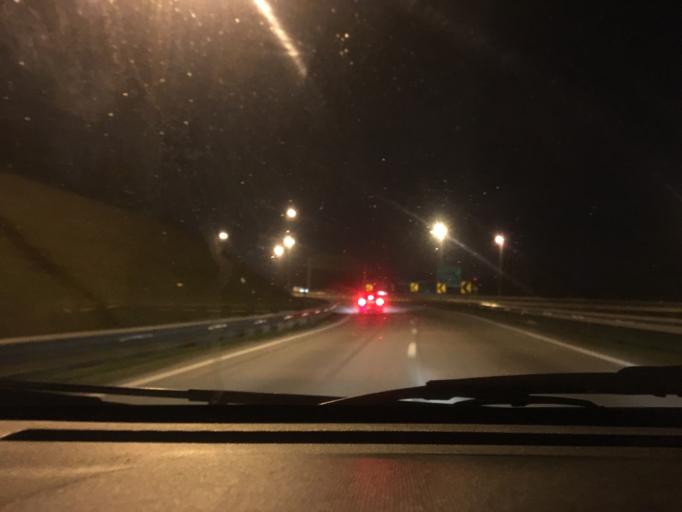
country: MY
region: Selangor
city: Kampong Baharu Balakong
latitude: 2.9825
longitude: 101.7314
